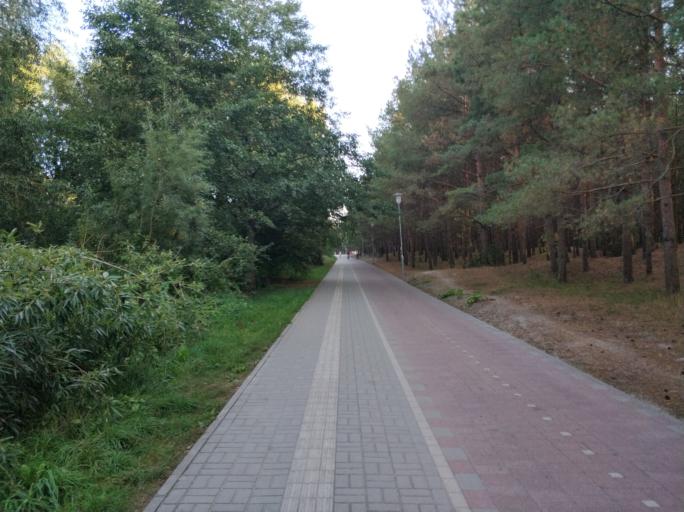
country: LV
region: Liepaja
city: Liepaja
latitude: 56.4930
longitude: 20.9975
